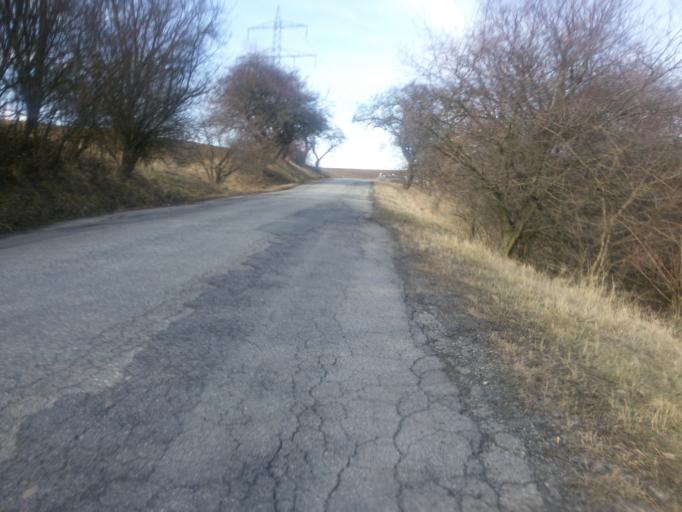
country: CZ
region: South Moravian
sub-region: Okres Brno-Venkov
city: Lomnice
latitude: 49.4168
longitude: 16.3996
